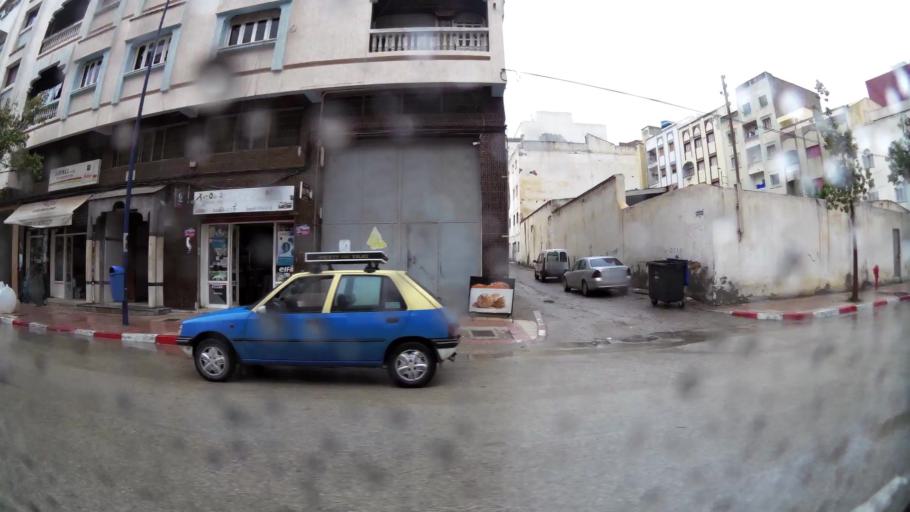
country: MA
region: Taza-Al Hoceima-Taounate
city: Al Hoceima
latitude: 35.2500
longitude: -3.9367
